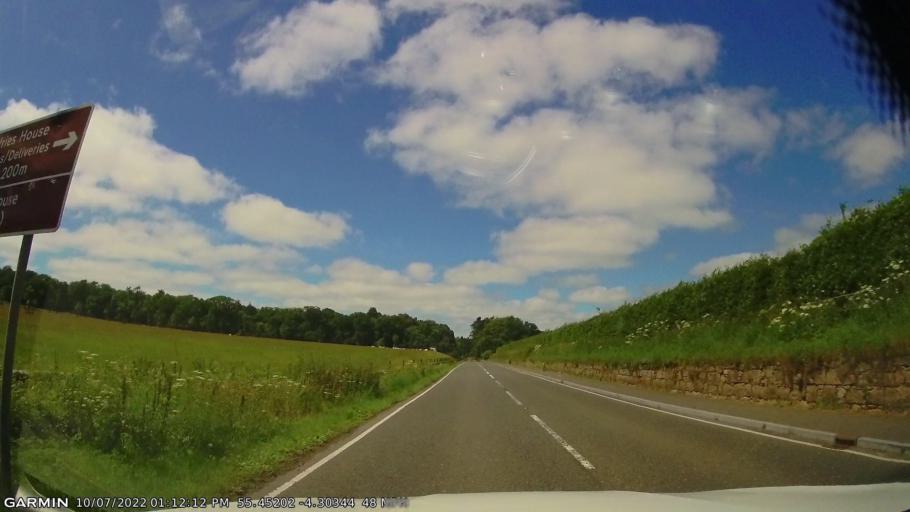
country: GB
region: Scotland
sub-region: East Ayrshire
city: Auchinleck
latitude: 55.4520
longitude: -4.3034
